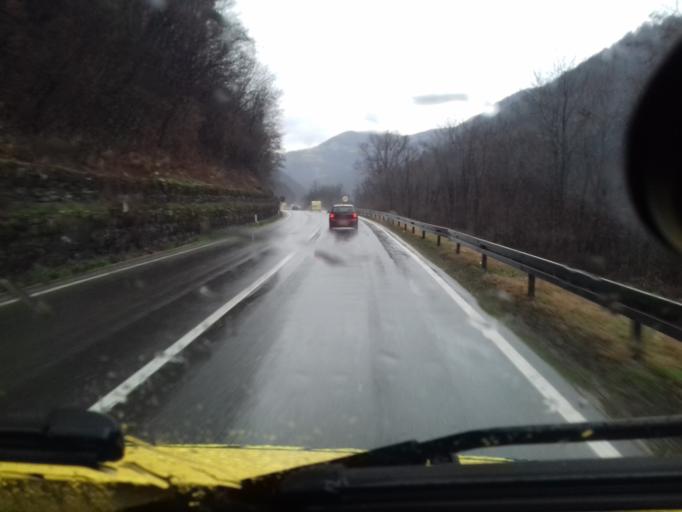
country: BA
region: Federation of Bosnia and Herzegovina
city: Lokvine
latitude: 44.2783
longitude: 17.8822
